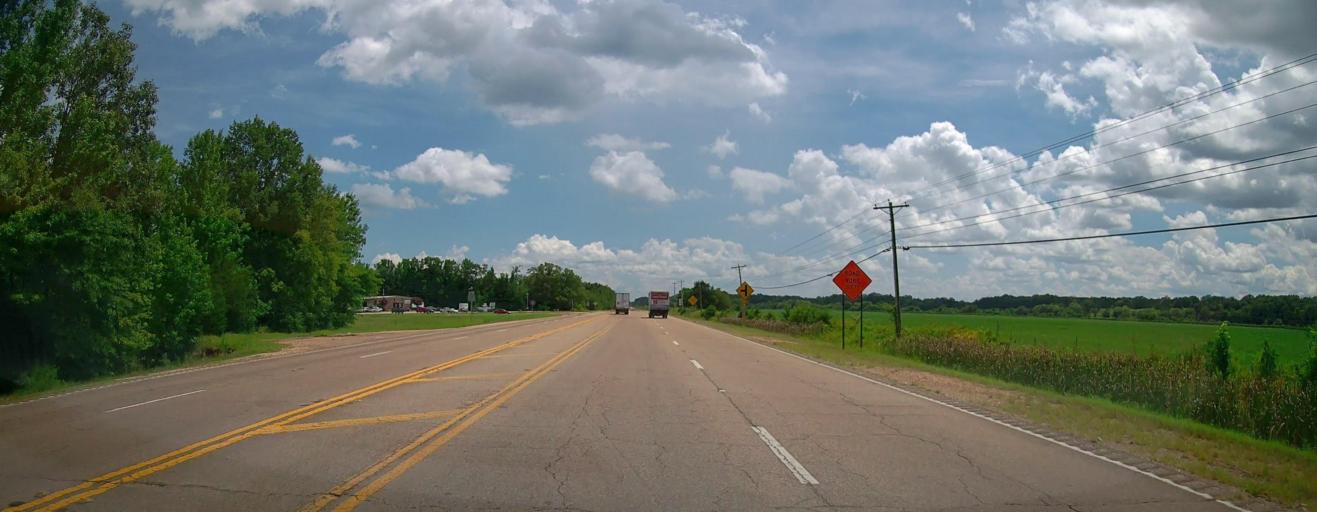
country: US
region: Mississippi
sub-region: Lee County
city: Shannon
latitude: 34.1537
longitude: -88.7195
